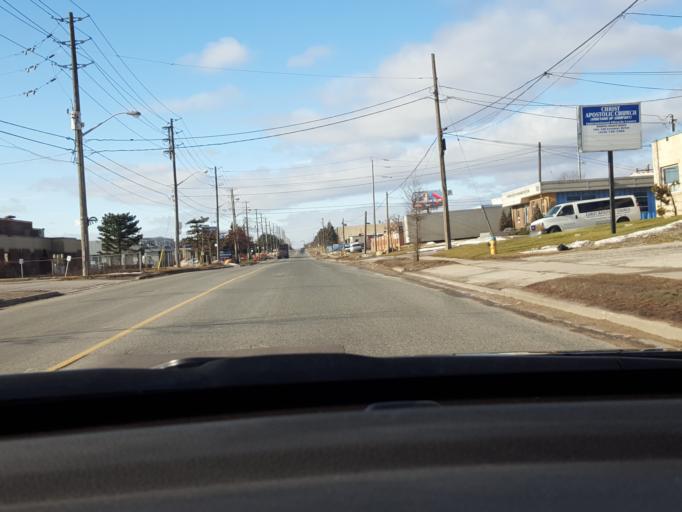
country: CA
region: Ontario
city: Concord
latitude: 43.7591
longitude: -79.5478
